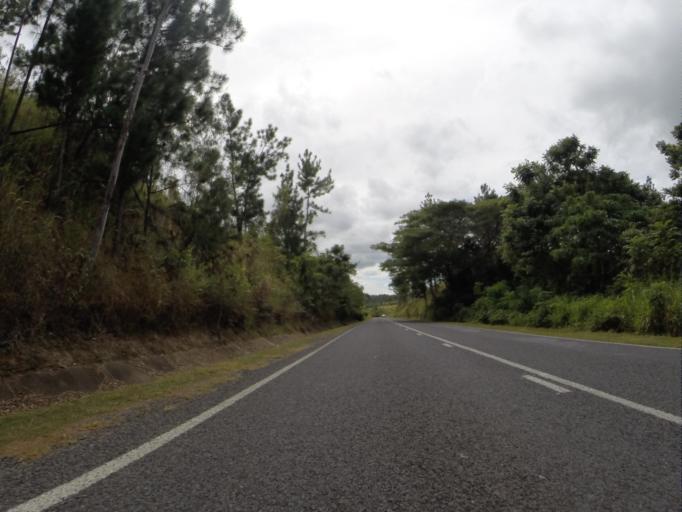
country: FJ
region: Western
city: Nadi
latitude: -17.9951
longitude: 177.3200
